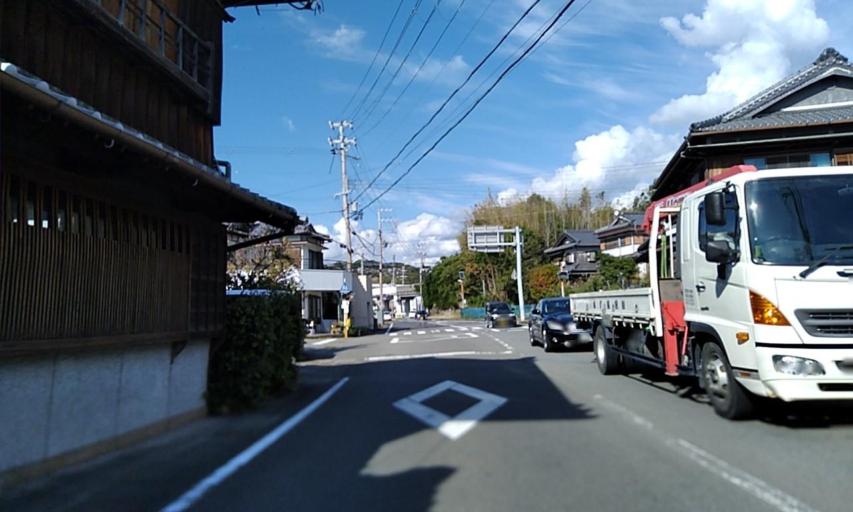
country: JP
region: Wakayama
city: Tanabe
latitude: 33.7491
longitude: 135.3524
